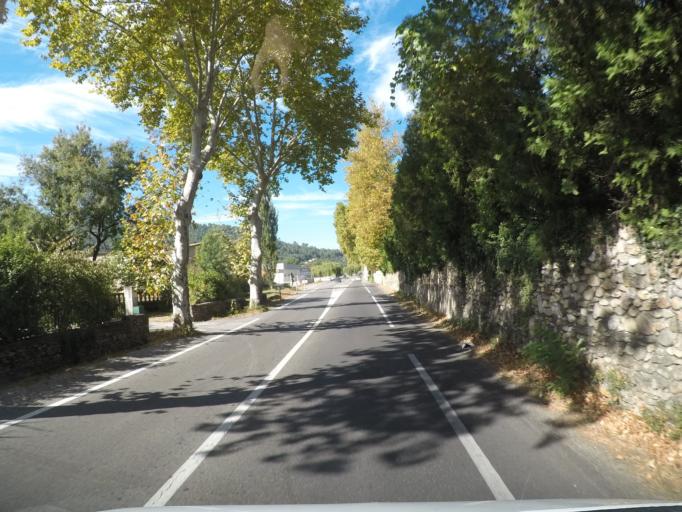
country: FR
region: Languedoc-Roussillon
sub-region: Departement du Gard
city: Anduze
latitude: 44.0595
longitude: 3.9740
